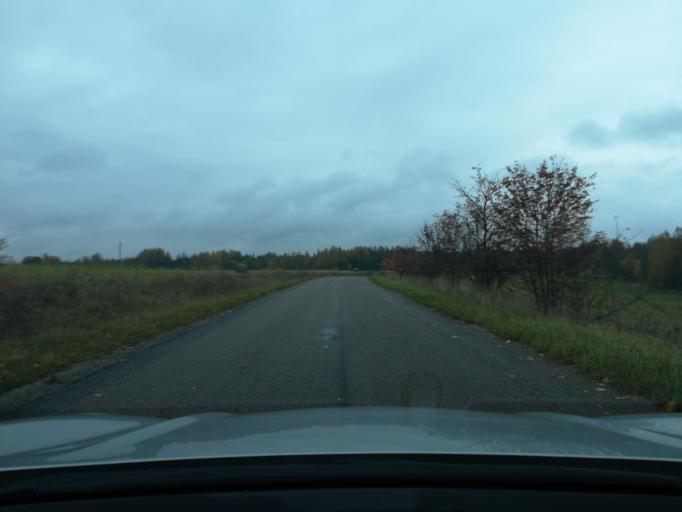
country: EE
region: Ida-Virumaa
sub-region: Johvi vald
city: Johvi
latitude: 59.1912
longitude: 27.5500
